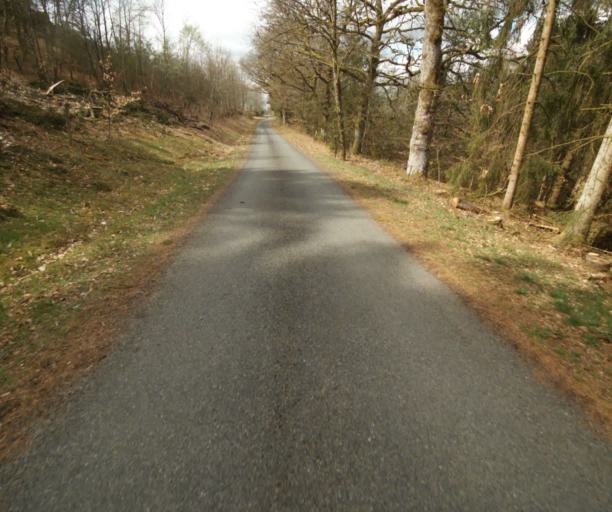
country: FR
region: Limousin
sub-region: Departement de la Correze
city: Correze
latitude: 45.3813
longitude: 1.9150
